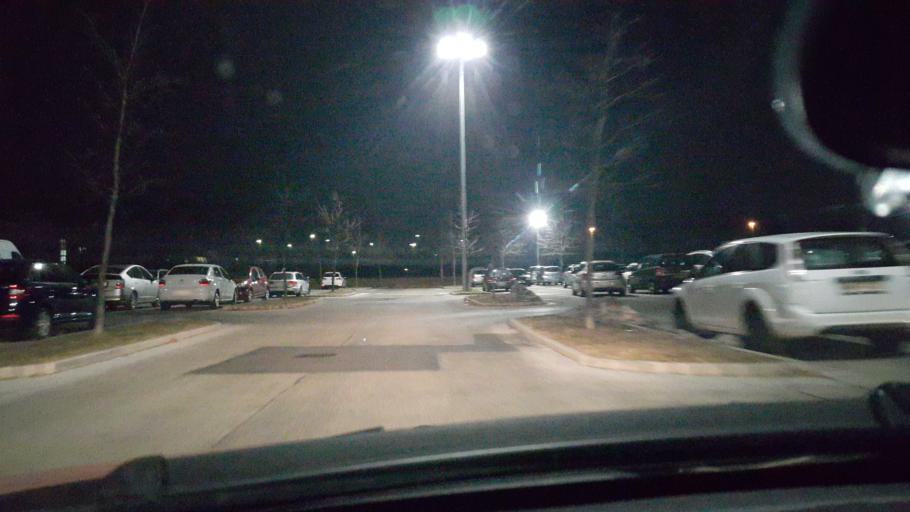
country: SI
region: Maribor
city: Razvanje
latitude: 46.5224
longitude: 15.6518
